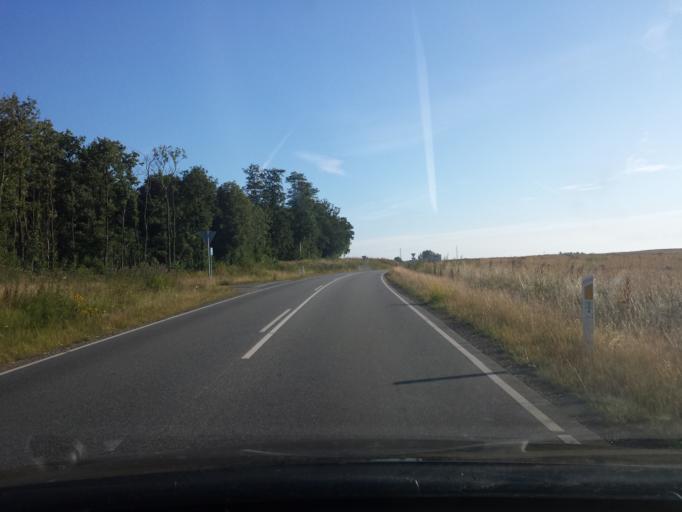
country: DK
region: South Denmark
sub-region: Sonderborg Kommune
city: Grasten
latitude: 54.9484
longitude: 9.6345
